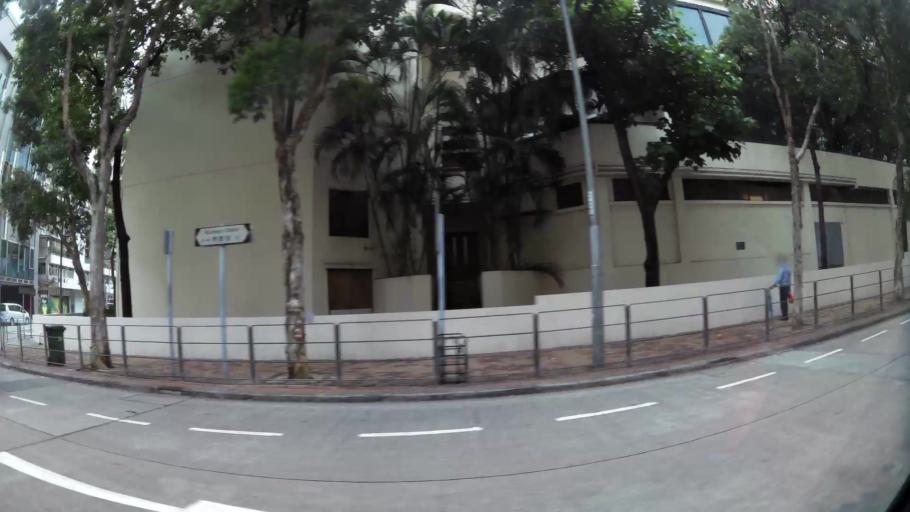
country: HK
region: Sham Shui Po
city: Sham Shui Po
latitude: 22.3266
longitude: 114.1688
